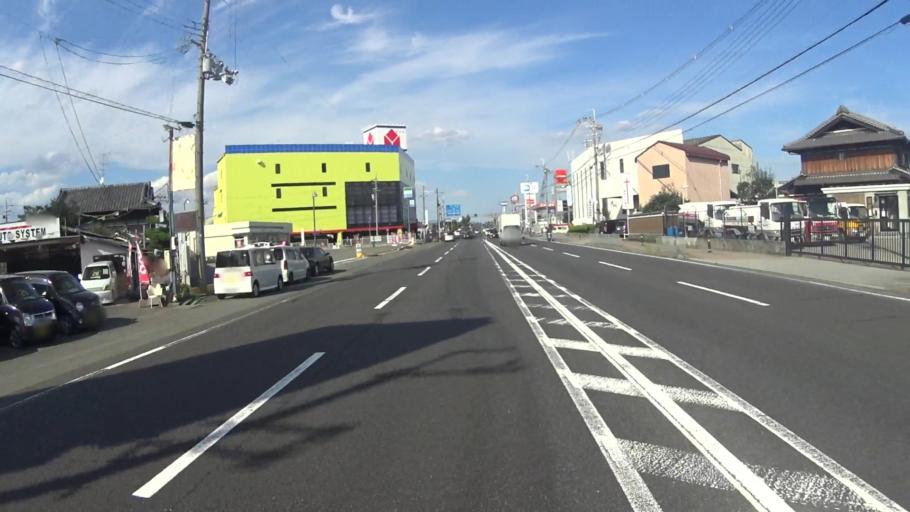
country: JP
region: Kyoto
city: Yawata
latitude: 34.8695
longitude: 135.7285
